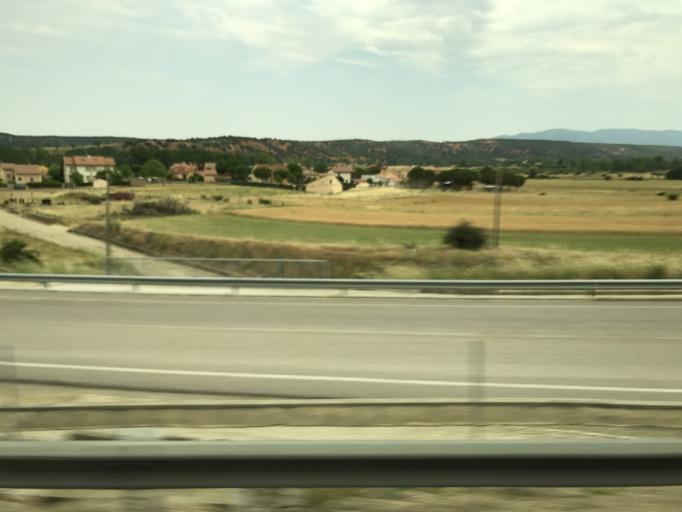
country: ES
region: Castille and Leon
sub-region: Provincia de Segovia
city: Castillejo de Mesleon
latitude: 41.2773
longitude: -3.6036
